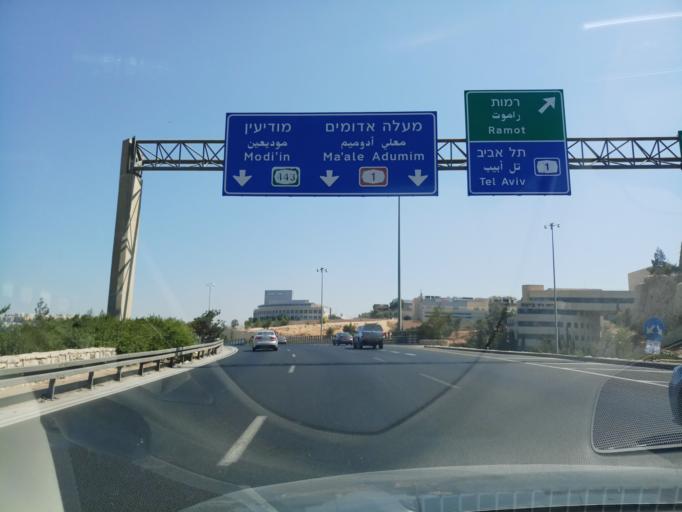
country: IL
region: Jerusalem
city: West Jerusalem
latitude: 31.8006
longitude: 35.2047
